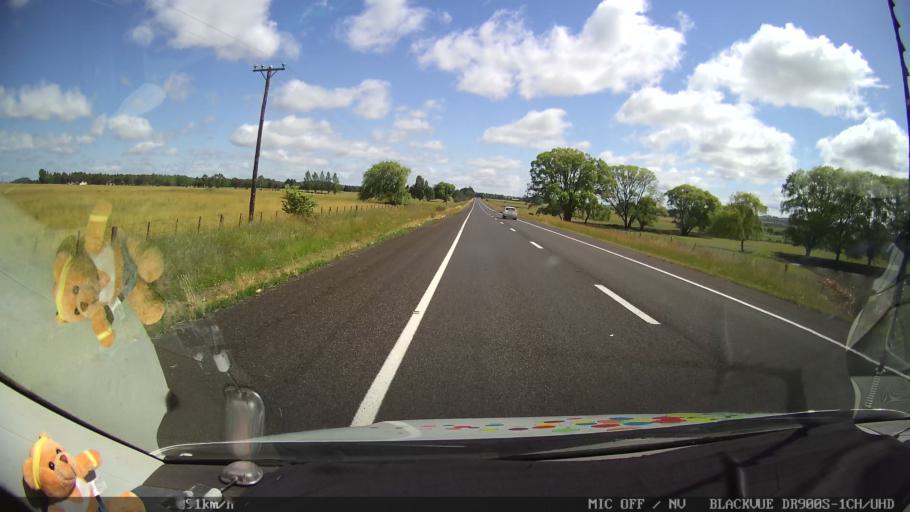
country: AU
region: New South Wales
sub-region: Glen Innes Severn
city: Glen Innes
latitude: -29.8314
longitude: 151.7377
